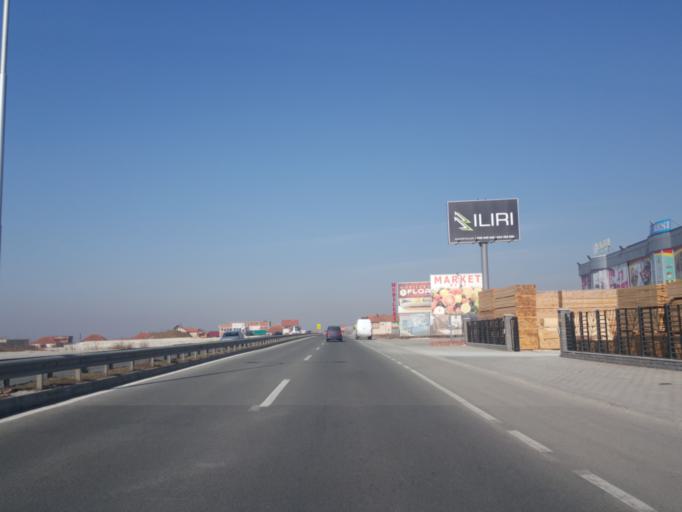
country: XK
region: Pristina
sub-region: Komuna e Obiliqit
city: Obiliq
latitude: 42.7427
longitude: 21.0500
